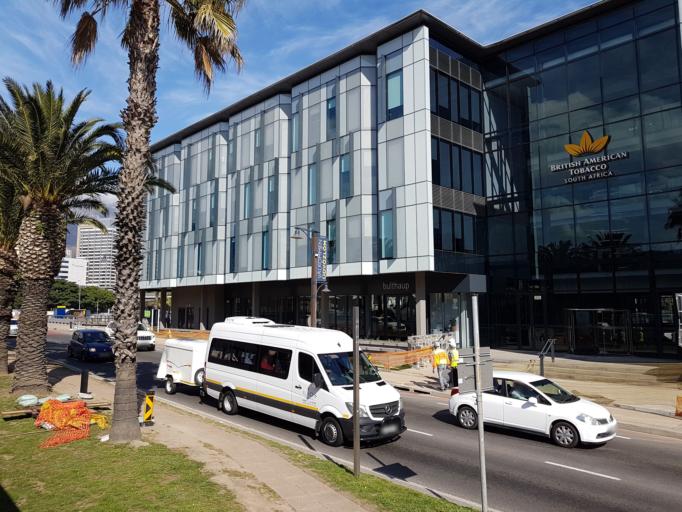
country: ZA
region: Western Cape
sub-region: City of Cape Town
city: Cape Town
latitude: -33.9129
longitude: 18.4232
